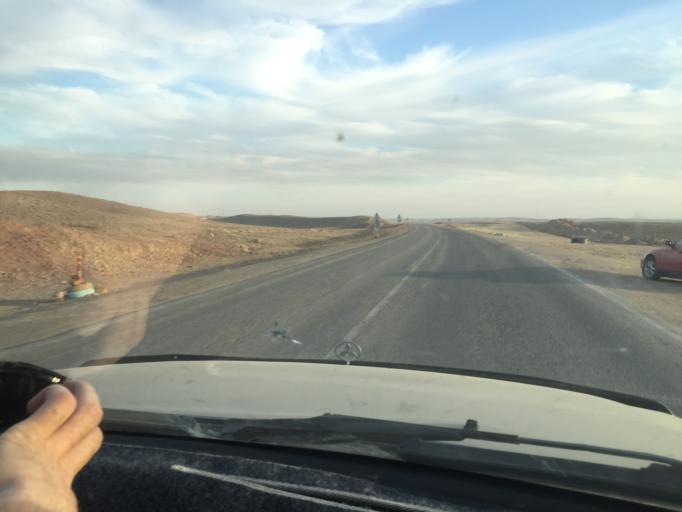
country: KZ
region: Almaty Oblysy
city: Ulken
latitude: 45.0817
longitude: 73.9712
